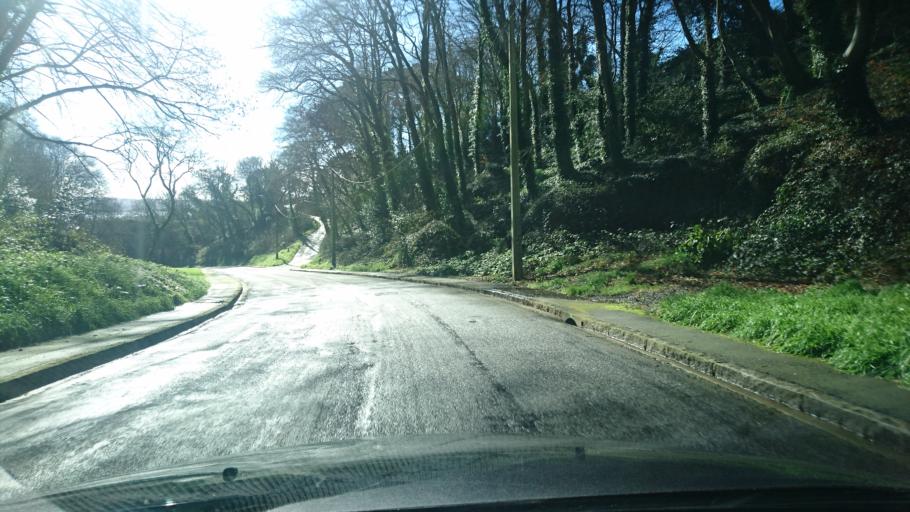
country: FR
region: Brittany
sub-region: Departement du Finistere
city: Brest
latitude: 48.3961
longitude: -4.4500
